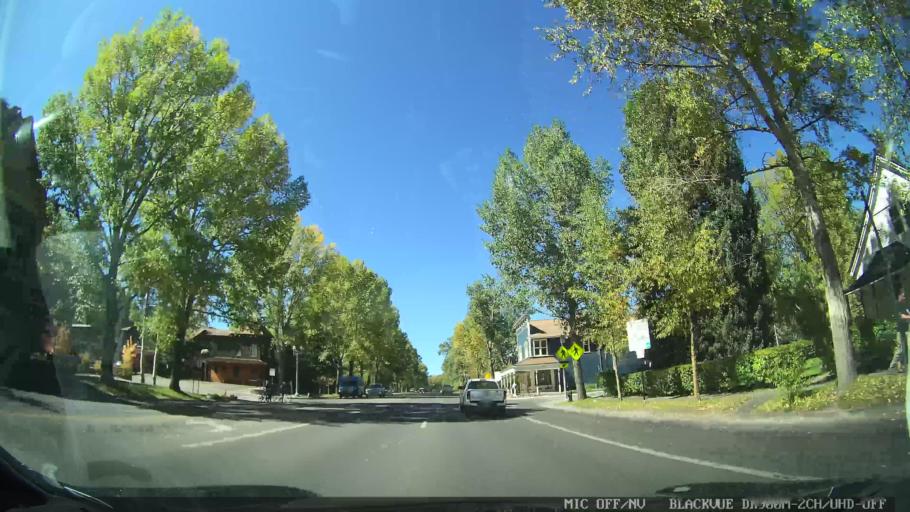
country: US
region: Colorado
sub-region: Pitkin County
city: Aspen
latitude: 39.1922
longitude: -106.8266
